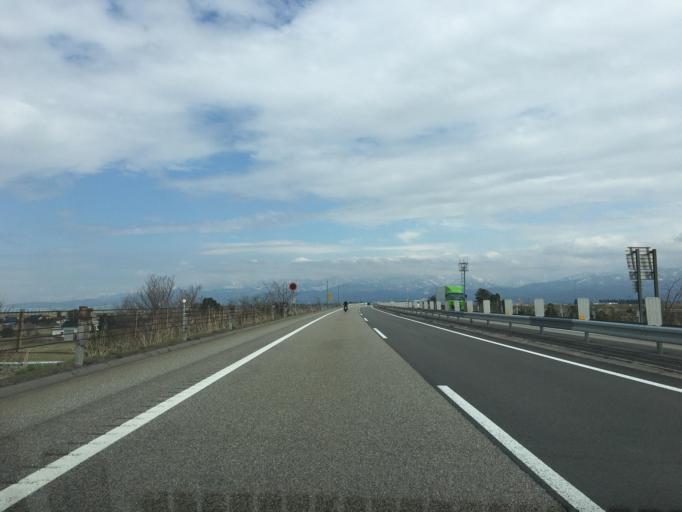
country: JP
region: Toyama
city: Toyama-shi
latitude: 36.6660
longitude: 137.2735
